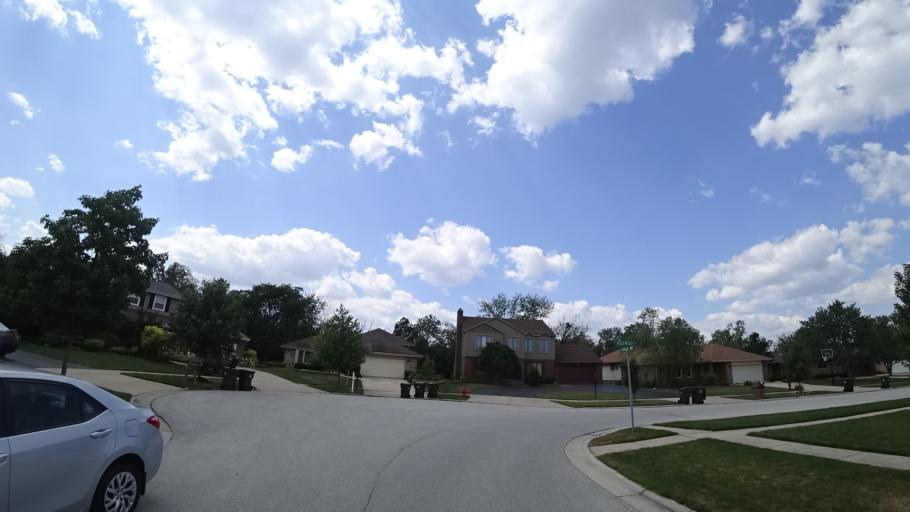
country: US
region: Illinois
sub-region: Cook County
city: Oak Forest
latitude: 41.6204
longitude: -87.7754
